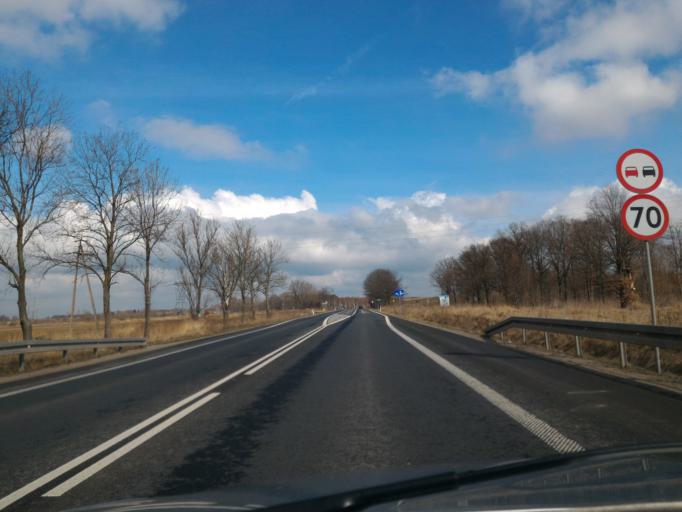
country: DE
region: Saxony
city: Ostritz
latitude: 51.0487
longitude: 14.9746
